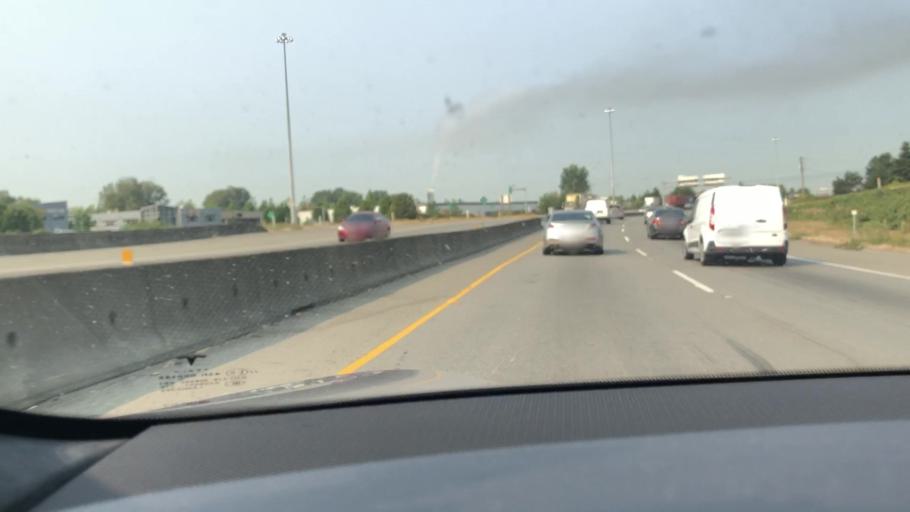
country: CA
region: British Columbia
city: Delta
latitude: 49.1698
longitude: -122.9737
